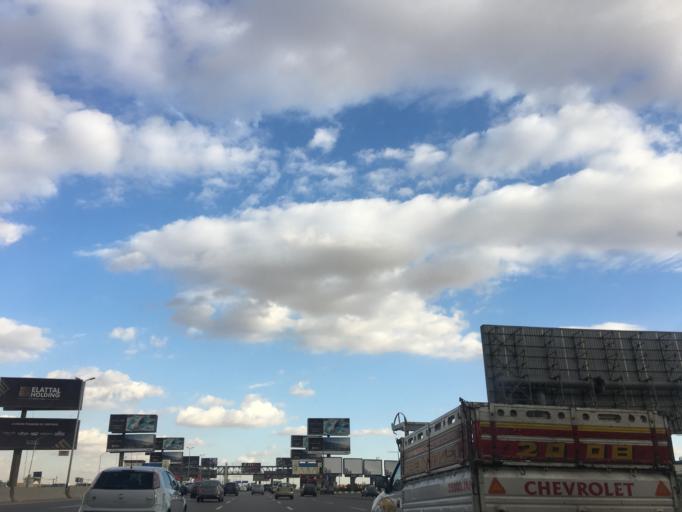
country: EG
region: Muhafazat al Qahirah
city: Cairo
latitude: 30.0175
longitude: 31.3900
